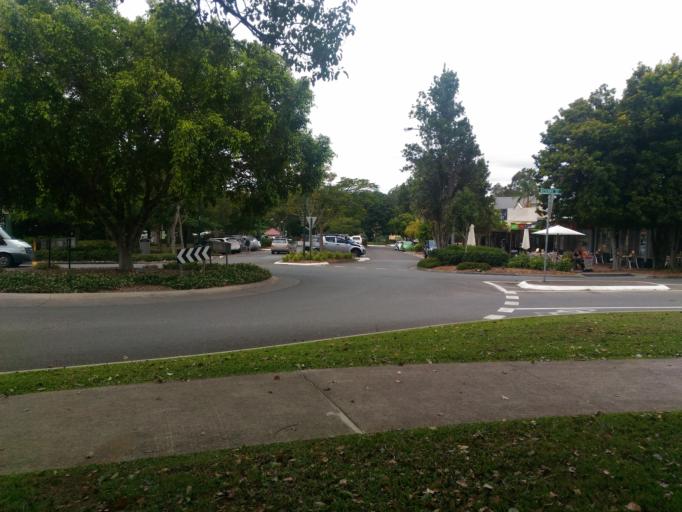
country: AU
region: Queensland
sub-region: Sunshine Coast
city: Black Mountain
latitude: -26.3660
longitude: 152.8547
